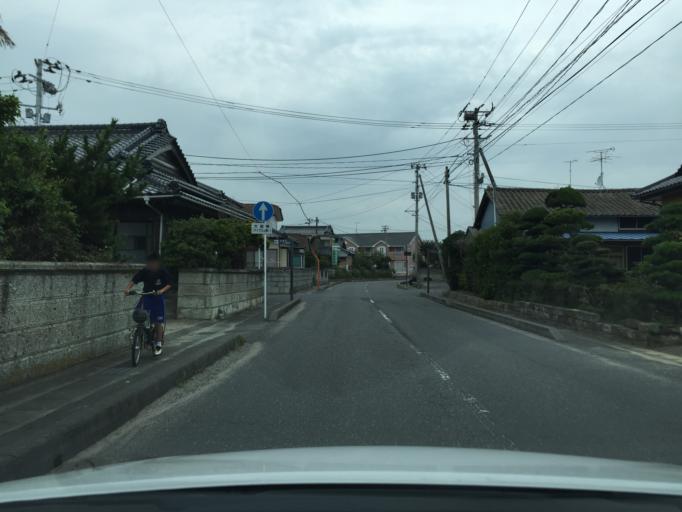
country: JP
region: Fukushima
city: Iwaki
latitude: 37.0146
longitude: 140.9702
